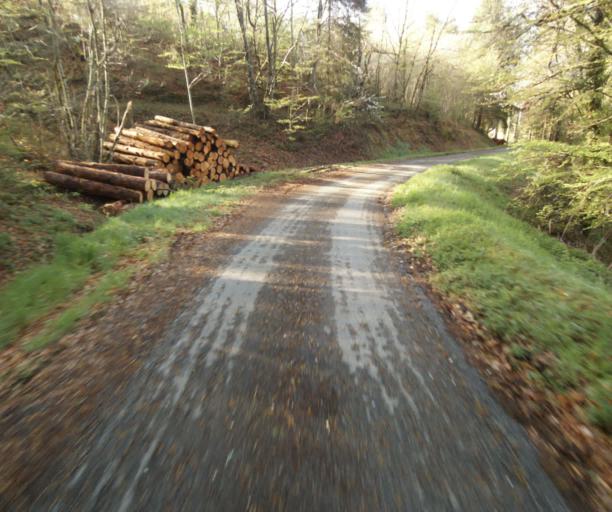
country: FR
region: Limousin
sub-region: Departement de la Correze
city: Laguenne
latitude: 45.2791
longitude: 1.8485
